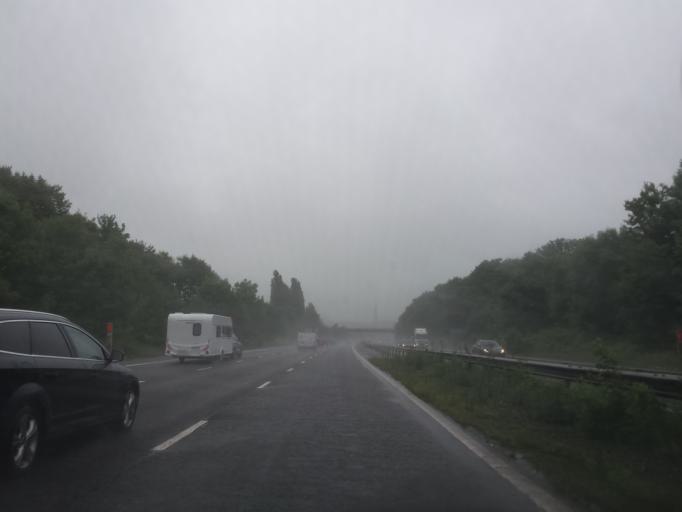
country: GB
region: England
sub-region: Leicestershire
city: Kirby Muxloe
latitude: 52.6522
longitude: -1.2386
